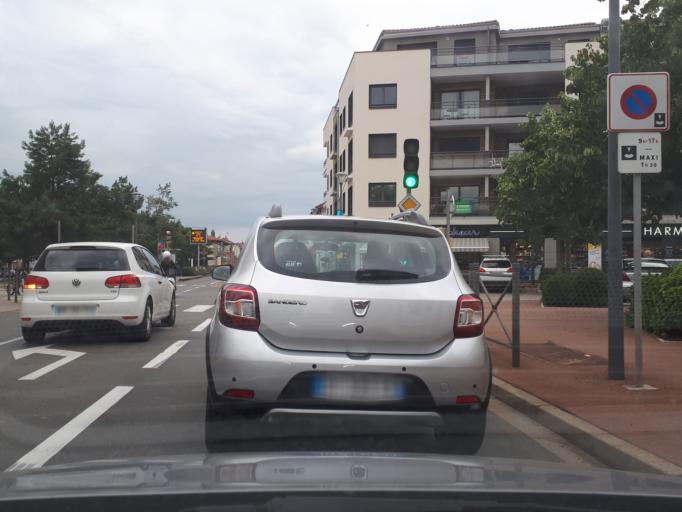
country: FR
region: Rhone-Alpes
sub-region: Departement de la Loire
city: Veauche
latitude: 45.5612
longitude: 4.2772
